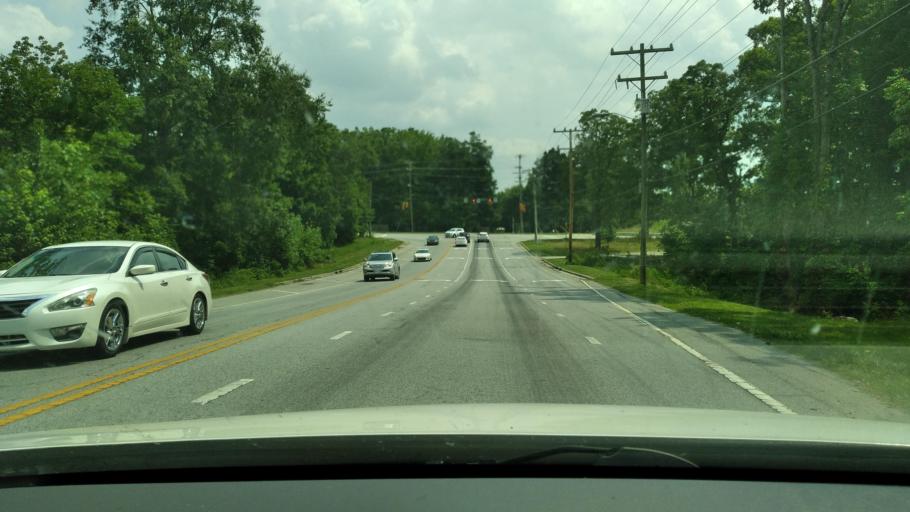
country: US
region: North Carolina
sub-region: Guilford County
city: Jamestown
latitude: 36.0372
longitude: -79.8890
